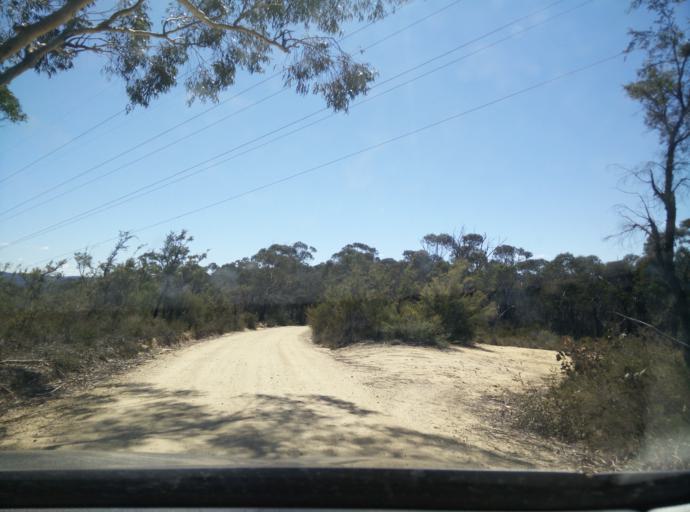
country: AU
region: New South Wales
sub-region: Blue Mountains Municipality
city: Blackheath
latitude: -33.5901
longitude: 150.2684
